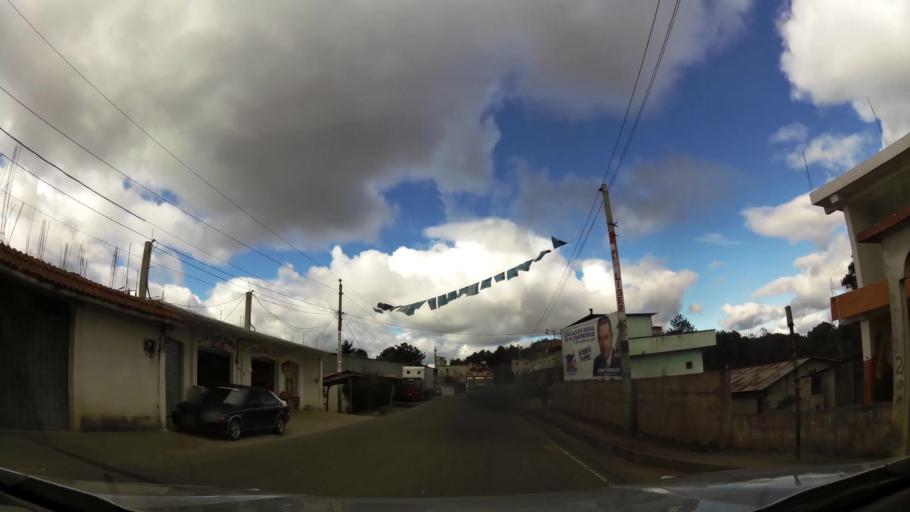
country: GT
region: Quiche
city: Chichicastenango
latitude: 14.9049
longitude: -91.1083
